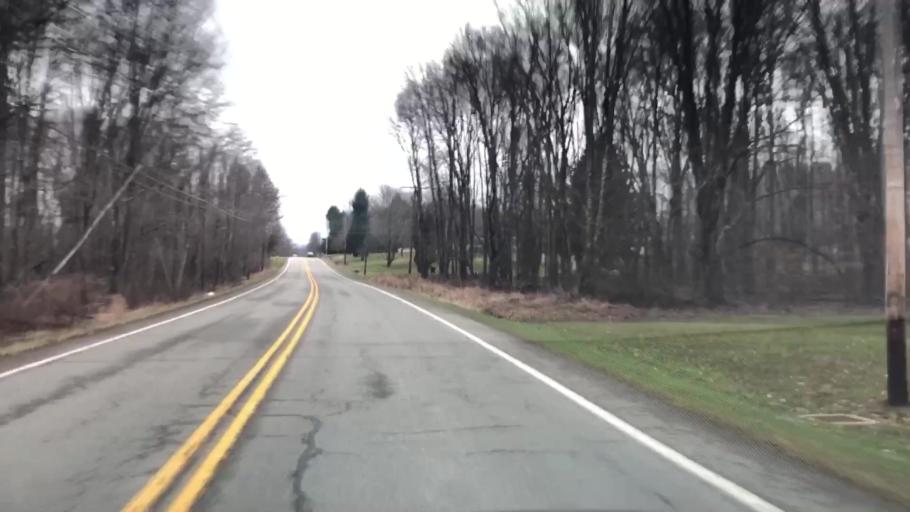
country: US
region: Pennsylvania
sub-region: Mercer County
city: Grove City
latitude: 41.1252
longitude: -80.0689
